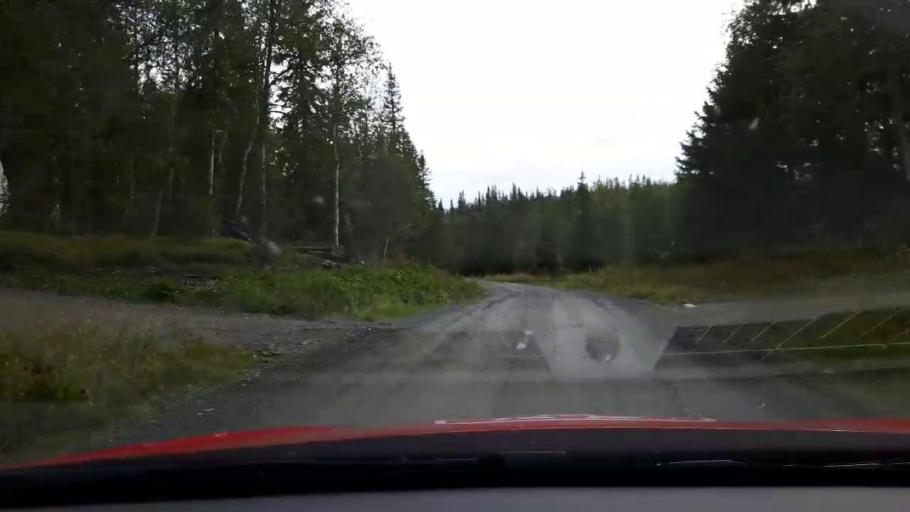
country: SE
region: Jaemtland
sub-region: Are Kommun
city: Are
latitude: 63.7750
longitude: 13.0700
